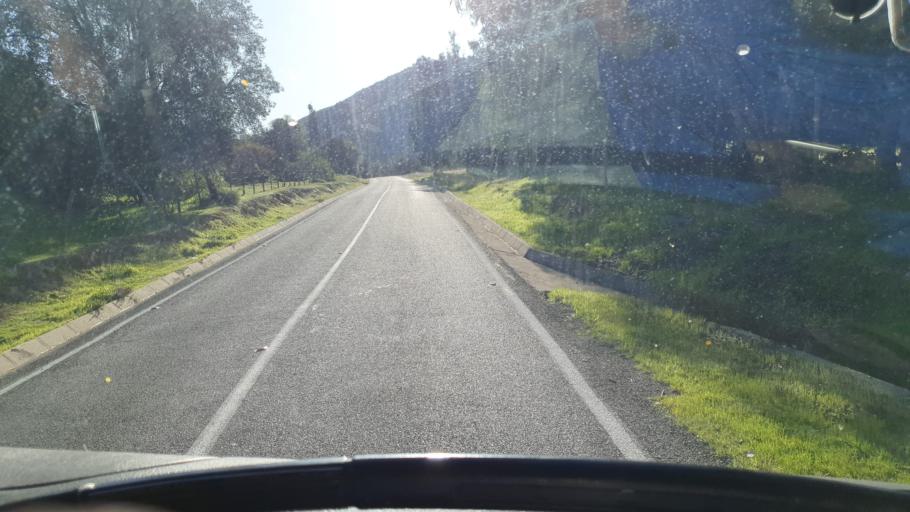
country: CL
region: Valparaiso
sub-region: Provincia de Marga Marga
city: Limache
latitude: -33.1984
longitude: -71.2291
